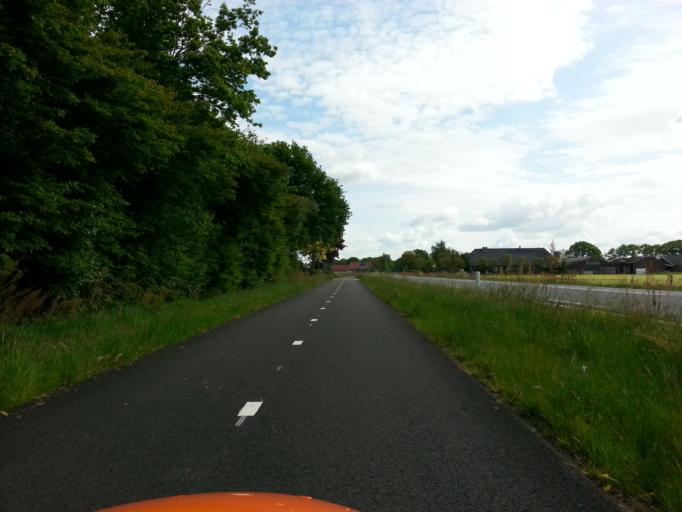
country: NL
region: Gelderland
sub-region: Gemeente Barneveld
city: Terschuur
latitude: 52.1090
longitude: 5.5285
